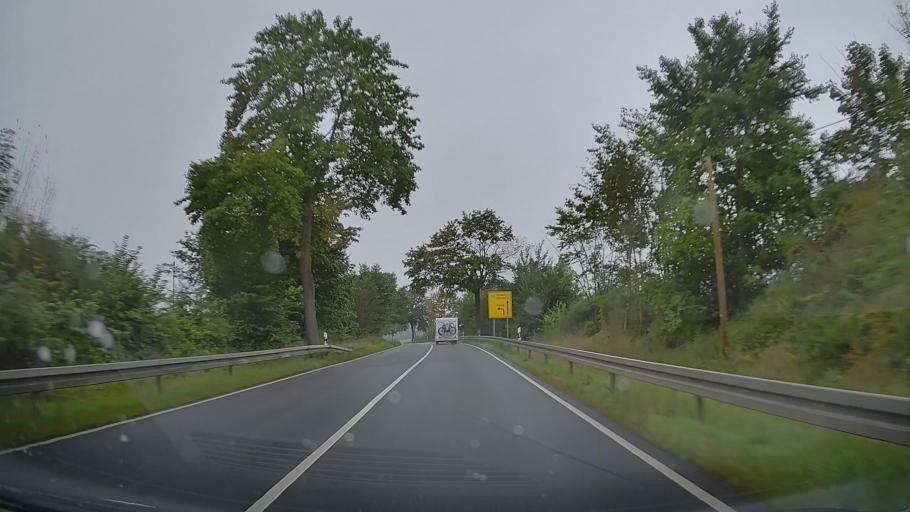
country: DE
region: Mecklenburg-Vorpommern
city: Gaegelow
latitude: 53.7114
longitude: 11.8691
